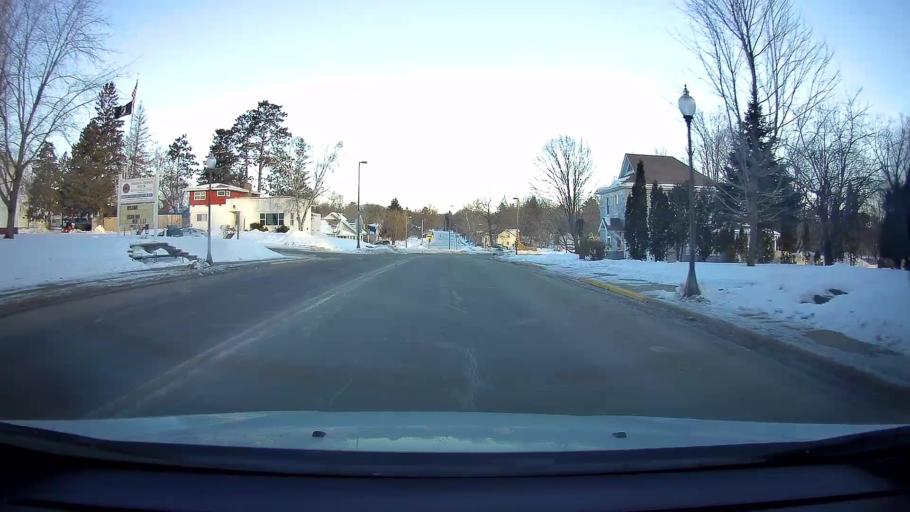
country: US
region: Wisconsin
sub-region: Barron County
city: Cumberland
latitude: 45.5391
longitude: -92.0219
